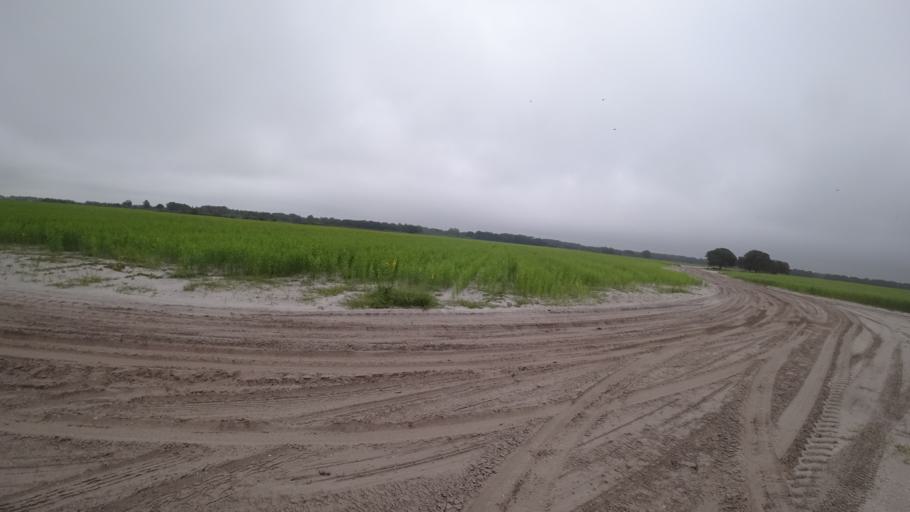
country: US
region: Florida
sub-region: Sarasota County
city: Warm Mineral Springs
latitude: 27.2912
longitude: -82.1603
